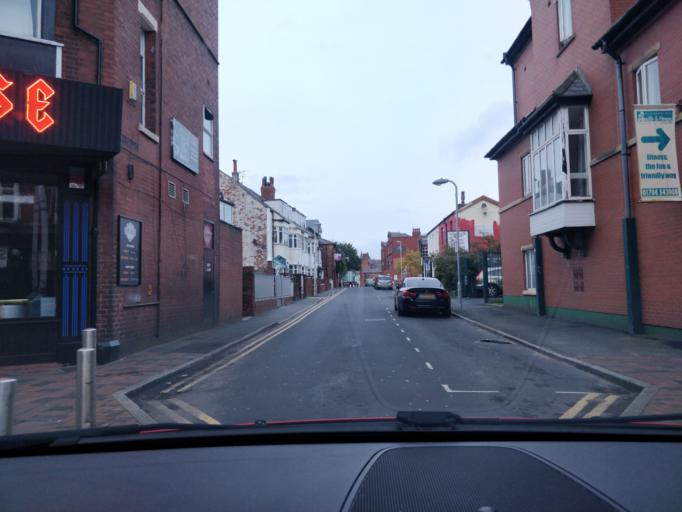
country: GB
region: England
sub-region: Sefton
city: Southport
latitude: 53.6479
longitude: -3.0084
